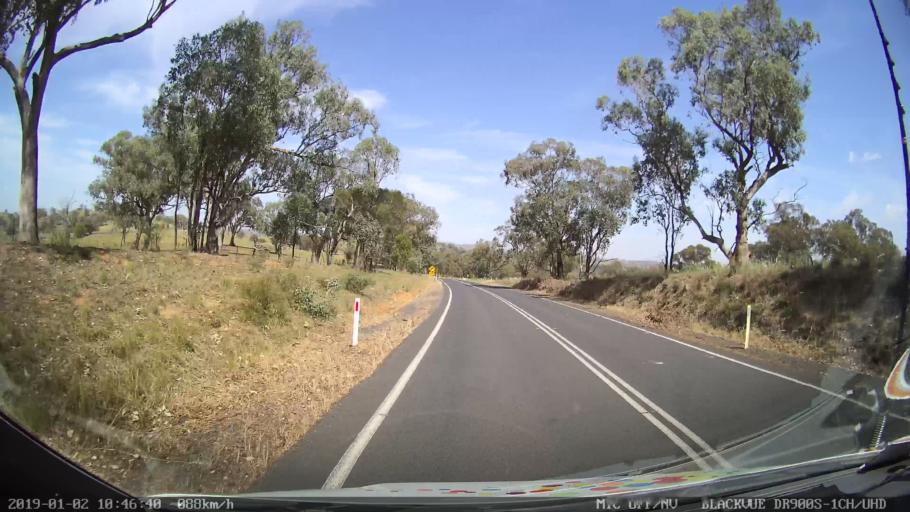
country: AU
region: New South Wales
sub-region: Cootamundra
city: Cootamundra
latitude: -34.7503
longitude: 148.2839
